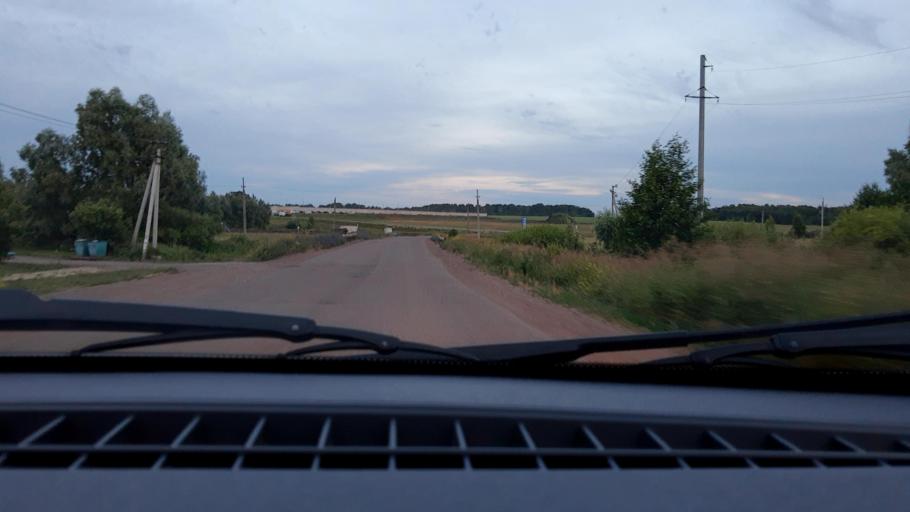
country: RU
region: Bashkortostan
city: Mikhaylovka
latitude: 54.7998
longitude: 55.7798
